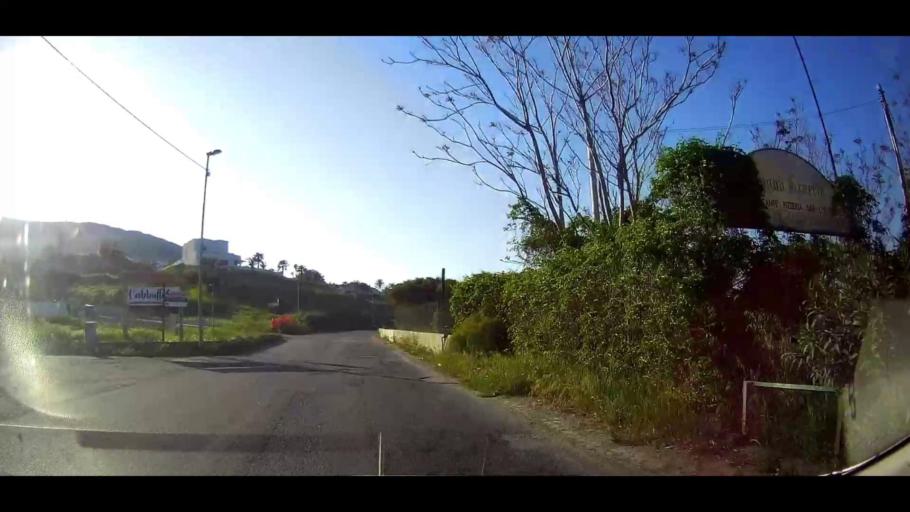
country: IT
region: Calabria
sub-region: Provincia di Crotone
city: Crotone
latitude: 39.0510
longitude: 17.1409
